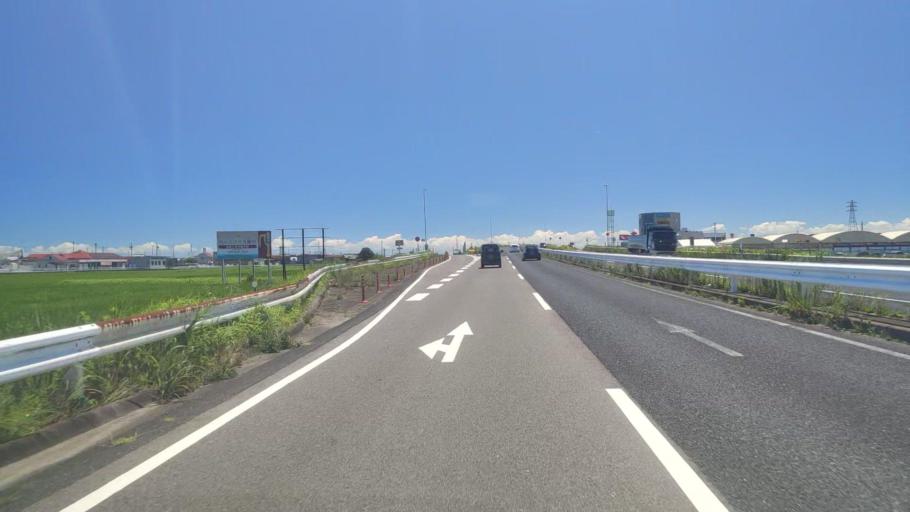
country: JP
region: Mie
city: Suzuka
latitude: 34.8779
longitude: 136.5957
